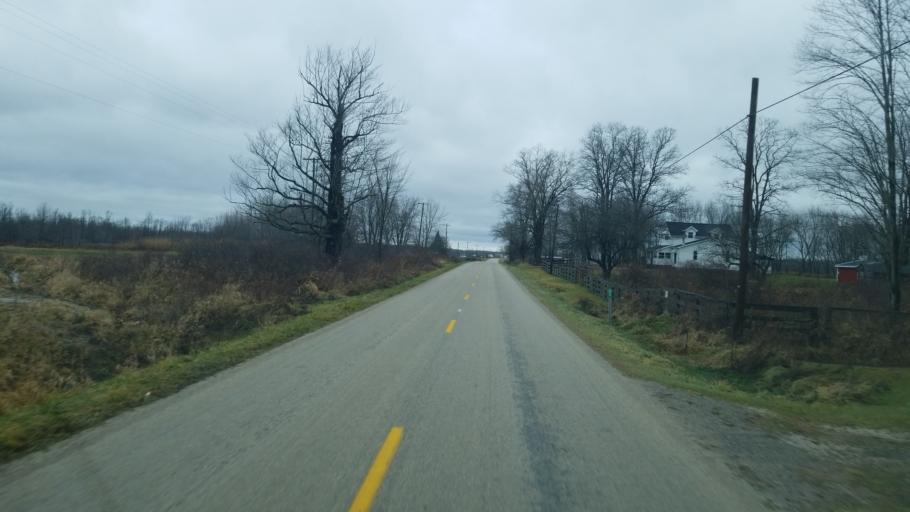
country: US
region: Ohio
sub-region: Ashtabula County
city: Andover
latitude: 41.6714
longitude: -80.6157
